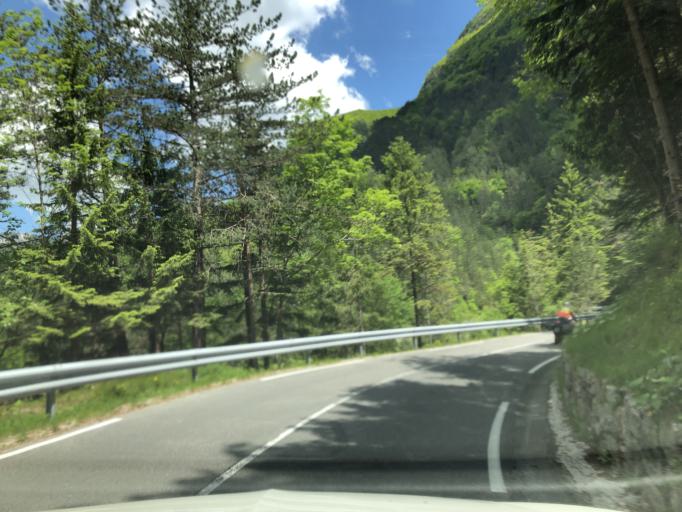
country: SI
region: Bovec
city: Bovec
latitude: 46.3869
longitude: 13.5879
